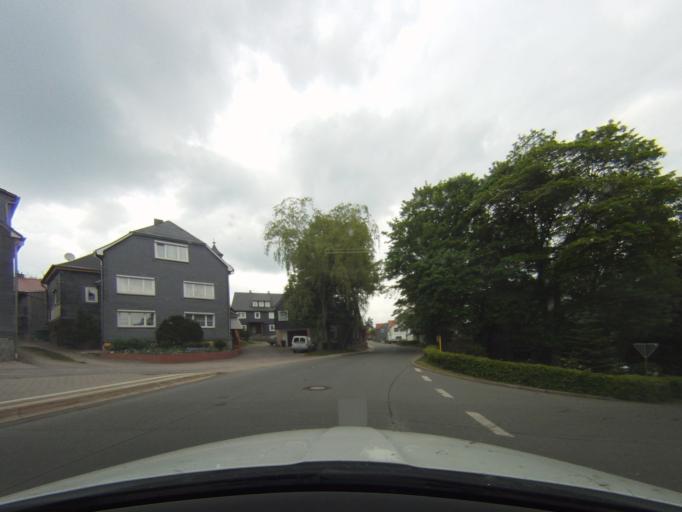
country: DE
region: Thuringia
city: Drobischau
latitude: 50.6294
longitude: 11.0714
